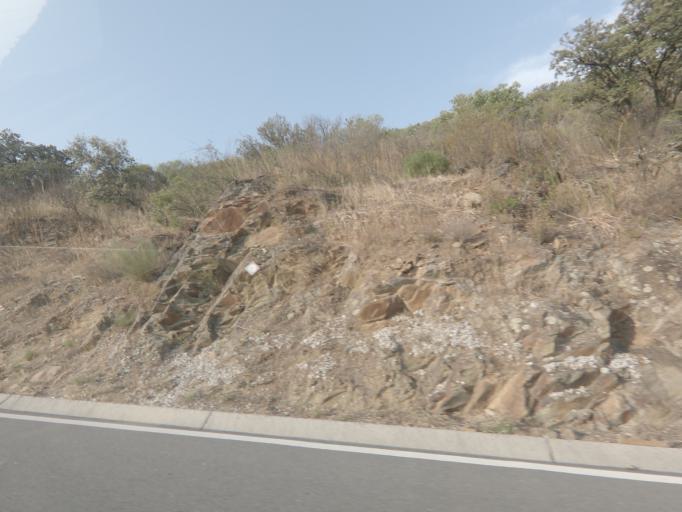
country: PT
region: Viseu
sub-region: Armamar
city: Armamar
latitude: 41.1513
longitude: -7.6352
